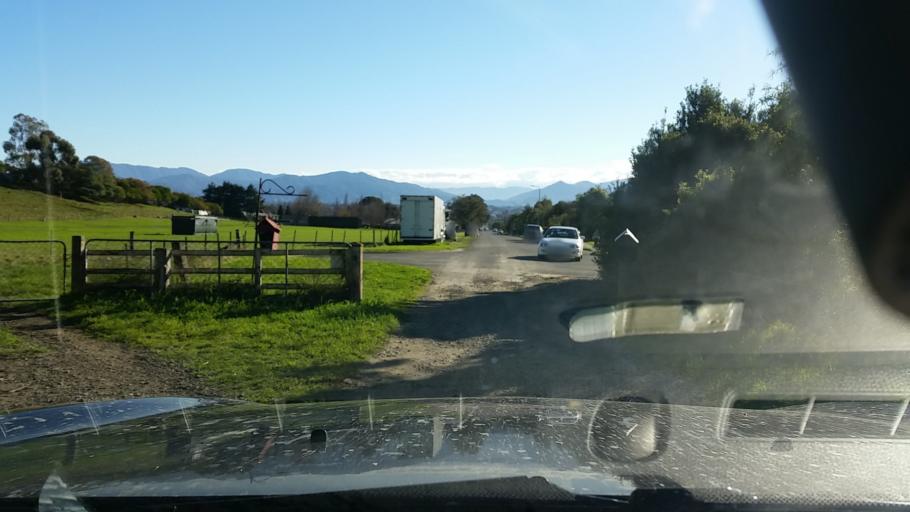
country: NZ
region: Marlborough
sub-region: Marlborough District
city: Blenheim
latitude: -41.5436
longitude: 173.9627
